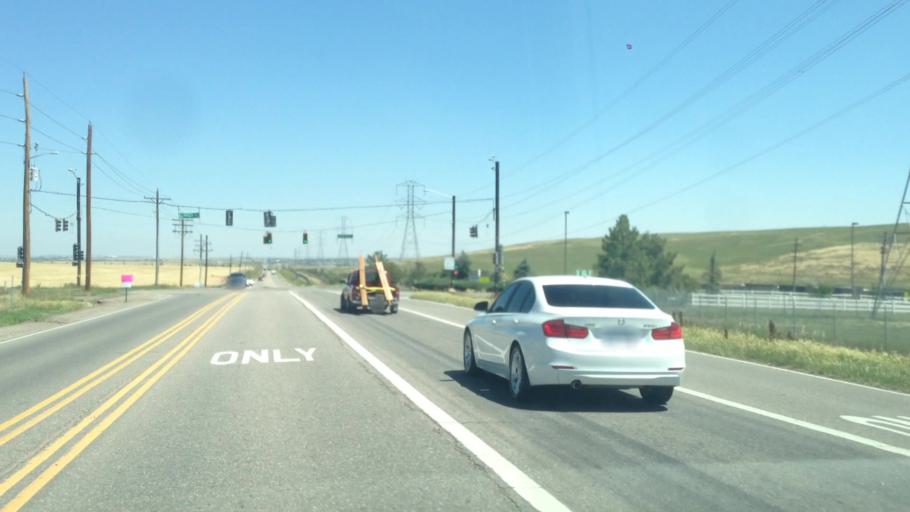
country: US
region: Colorado
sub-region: Arapahoe County
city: Dove Valley
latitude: 39.6521
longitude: -104.7162
